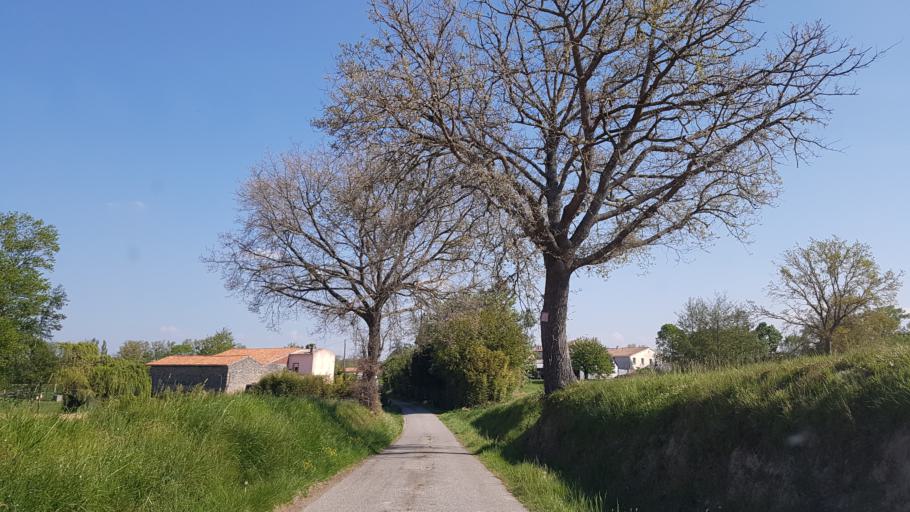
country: FR
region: Midi-Pyrenees
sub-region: Departement de l'Ariege
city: La Tour-du-Crieu
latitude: 43.0952
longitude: 1.7186
